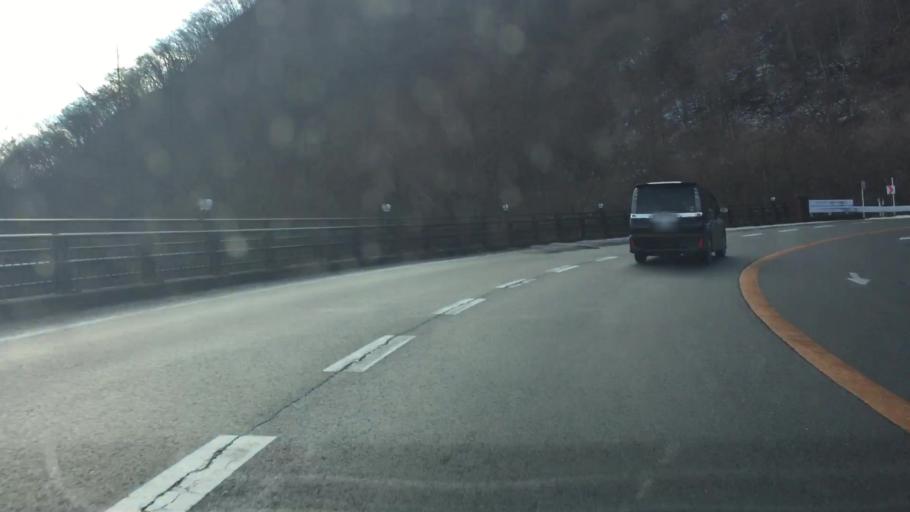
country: JP
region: Nagano
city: Saku
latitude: 36.3031
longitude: 138.6604
